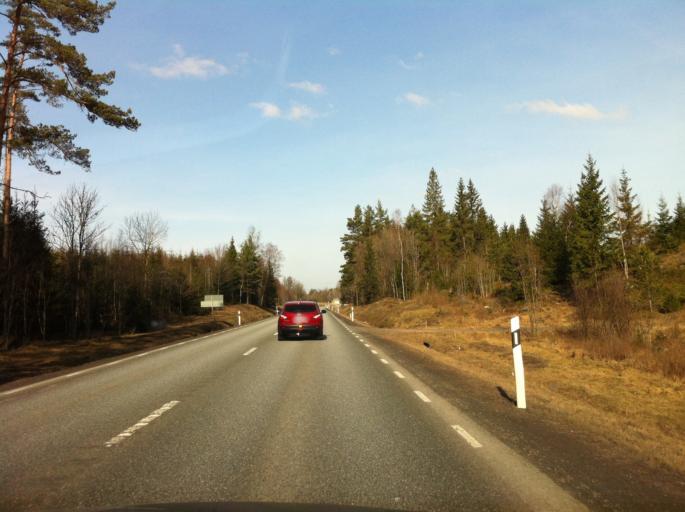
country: SE
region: Joenkoeping
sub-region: Mullsjo Kommun
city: Mullsjoe
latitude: 57.9874
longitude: 13.8284
